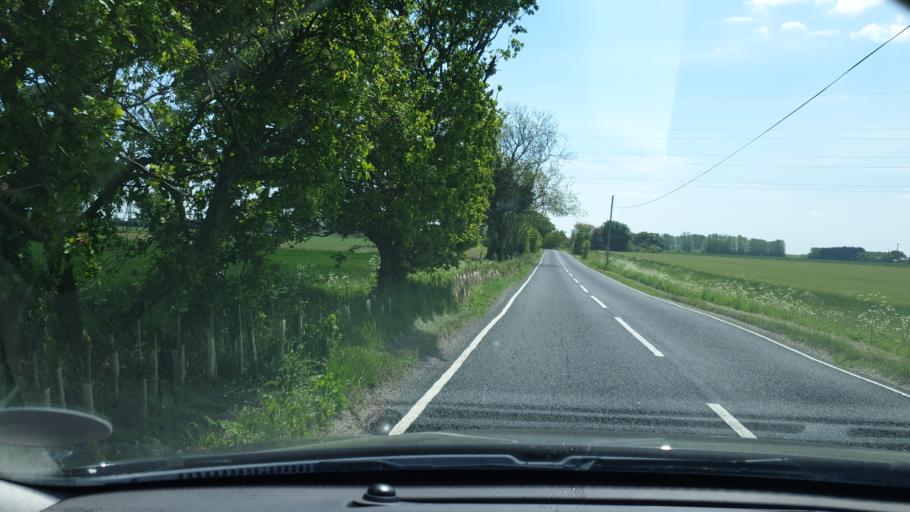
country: GB
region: England
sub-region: Essex
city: Manningtree
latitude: 51.9049
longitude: 1.0599
